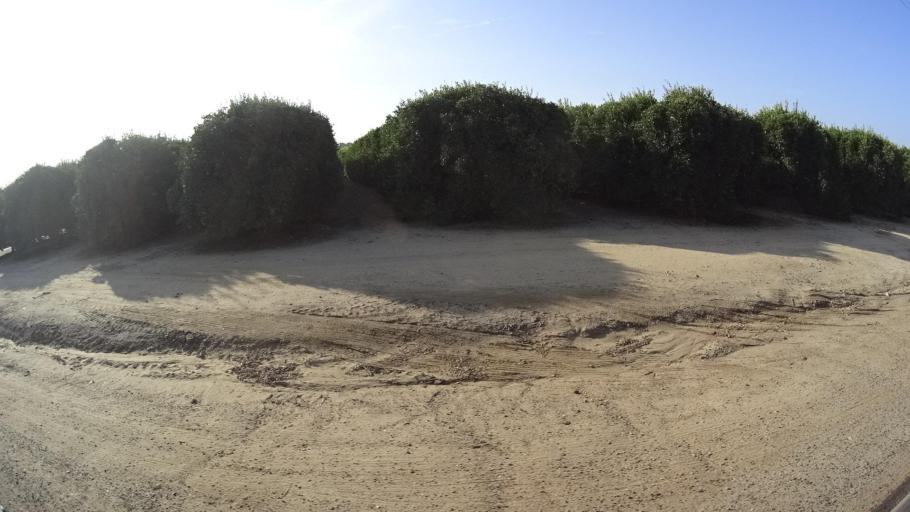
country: US
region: California
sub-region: Kern County
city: McFarland
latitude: 35.6692
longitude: -119.1253
